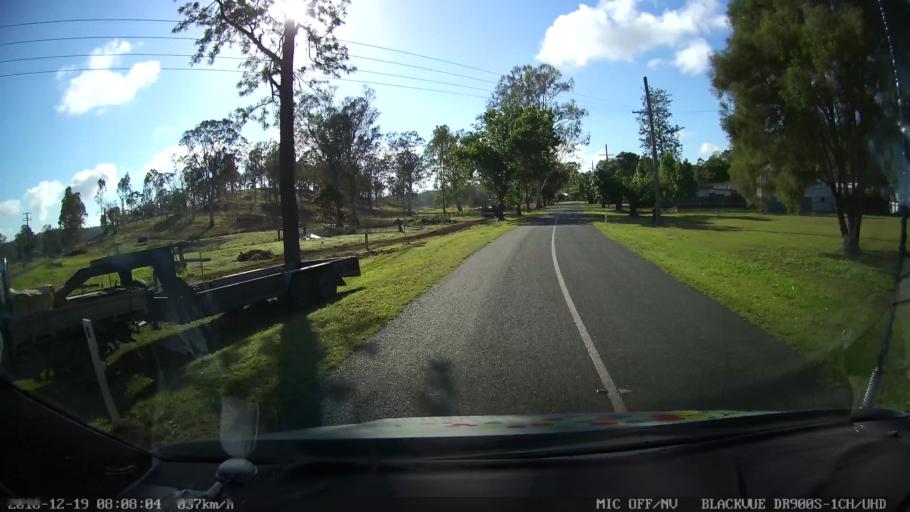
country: AU
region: Queensland
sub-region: Logan
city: Cedar Vale
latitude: -28.2110
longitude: 152.8681
